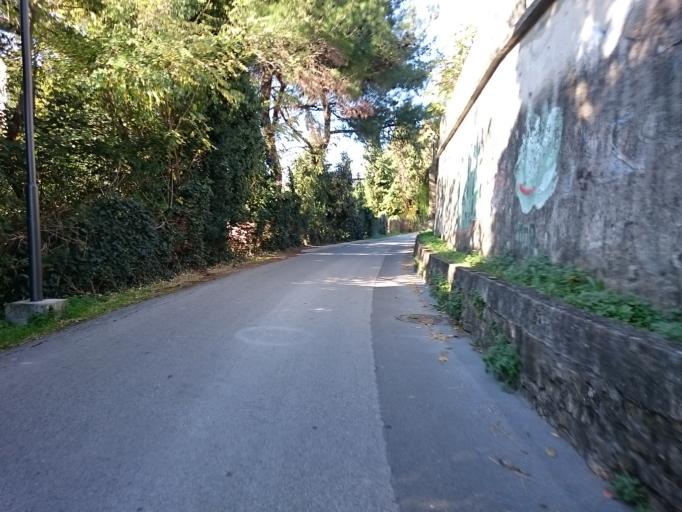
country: SI
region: Piran-Pirano
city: Lucija
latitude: 45.5085
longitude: 13.5997
